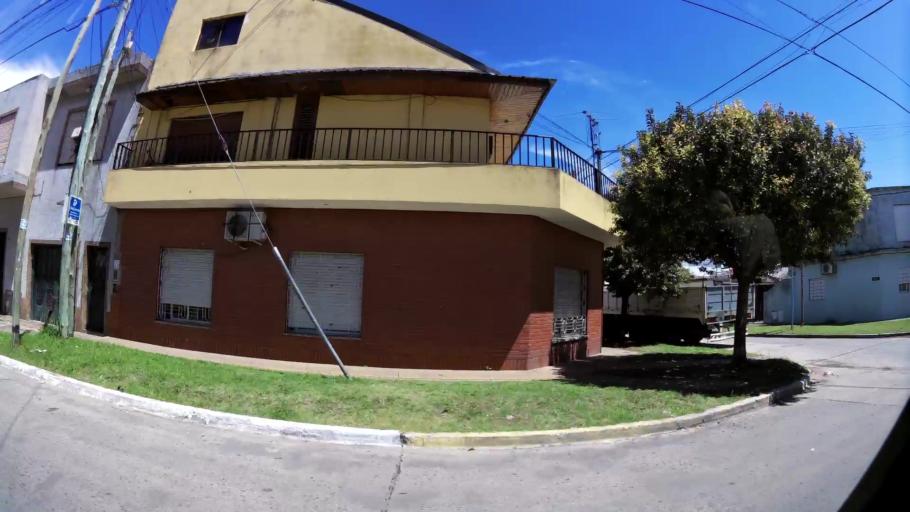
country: AR
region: Buenos Aires
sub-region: Partido de Quilmes
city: Quilmes
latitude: -34.7456
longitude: -58.2811
